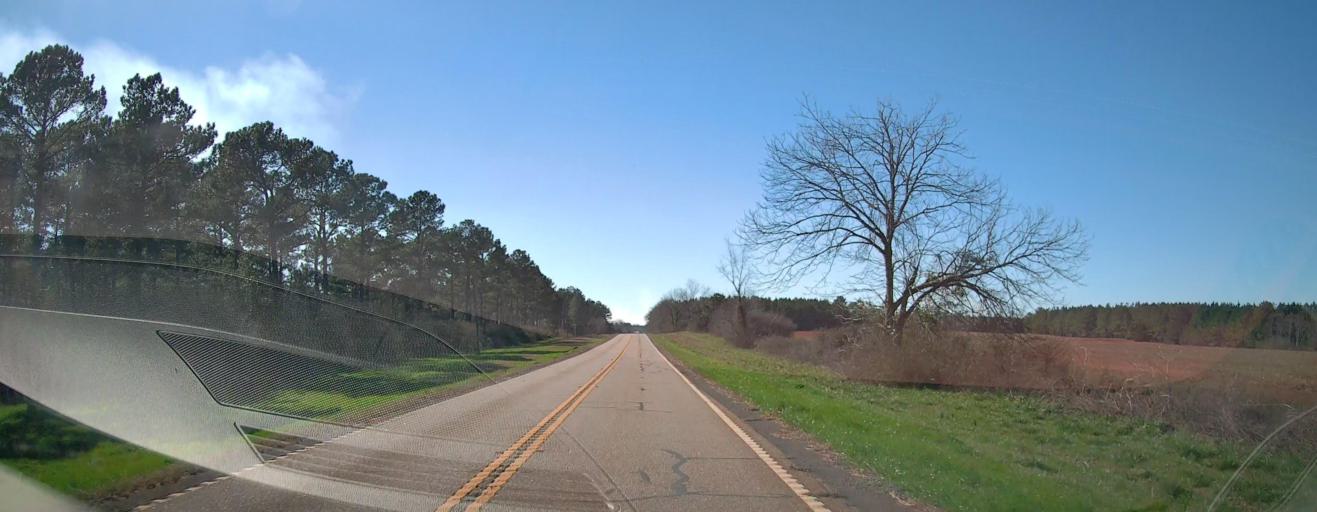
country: US
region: Georgia
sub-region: Sumter County
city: Americus
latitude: 32.1888
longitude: -84.1844
